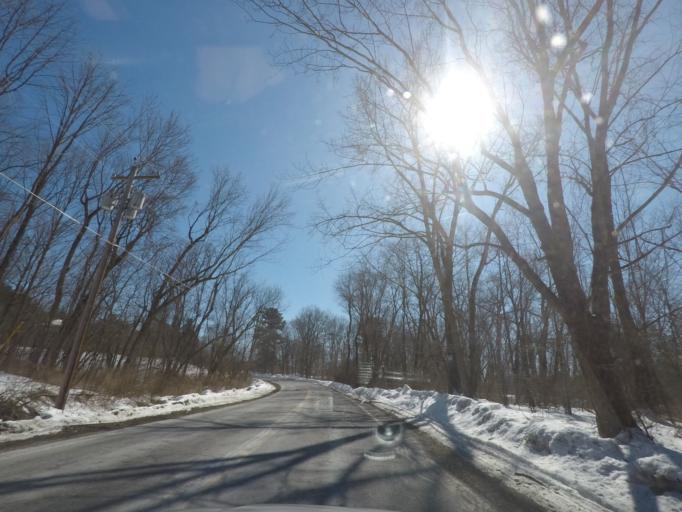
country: US
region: New York
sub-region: Saratoga County
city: Schuylerville
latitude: 43.1228
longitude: -73.5789
